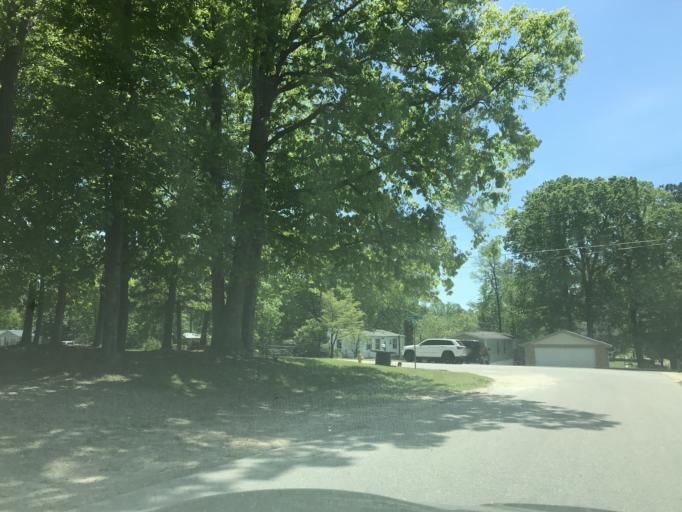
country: US
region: North Carolina
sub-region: Wake County
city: Raleigh
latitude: 35.8248
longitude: -78.5737
